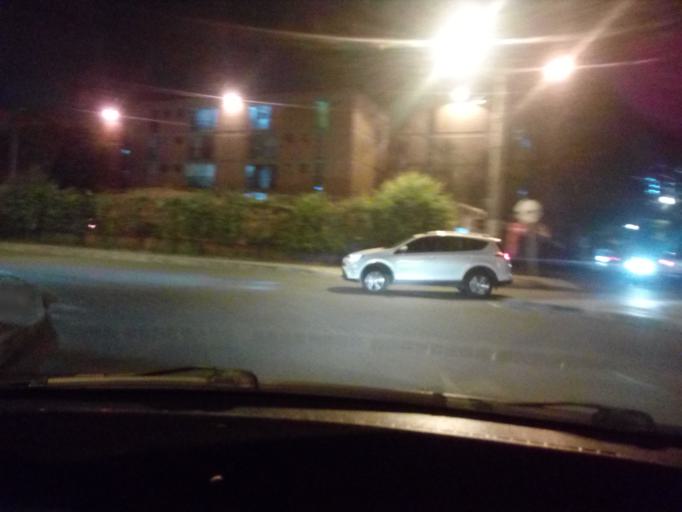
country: CO
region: Antioquia
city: Itagui
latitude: 6.1931
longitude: -75.5930
